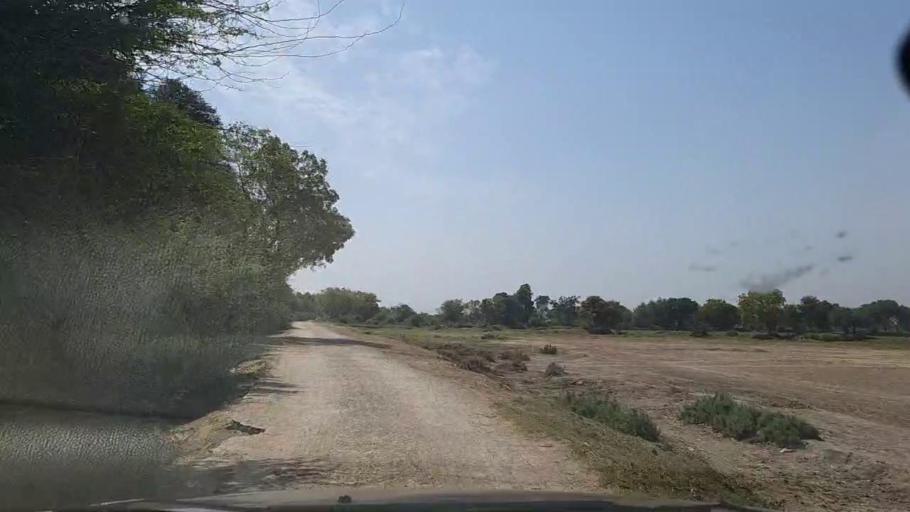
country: PK
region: Sindh
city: Mirpur Batoro
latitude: 24.6477
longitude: 68.1515
